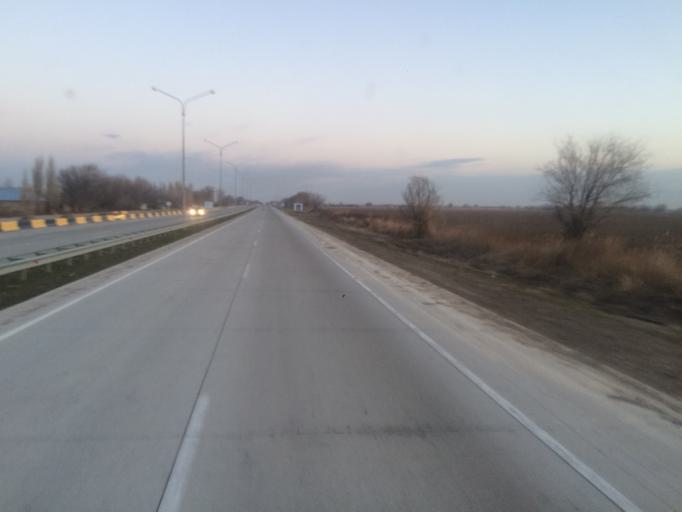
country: KZ
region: Ongtustik Qazaqstan
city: Shayan
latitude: 42.9604
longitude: 68.8884
